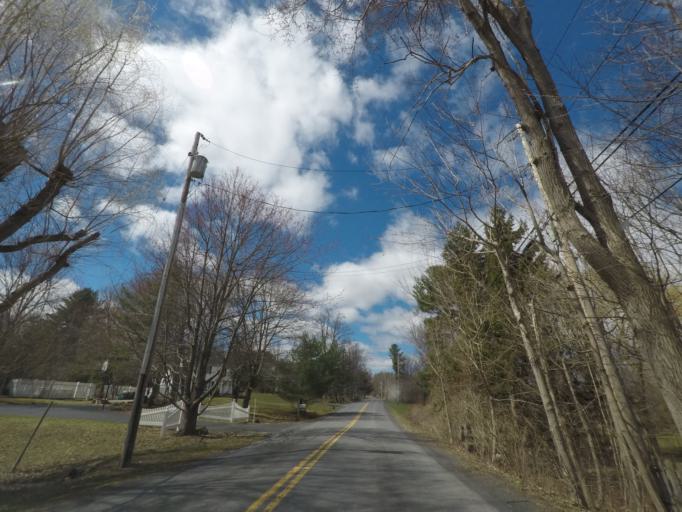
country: US
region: New York
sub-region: Albany County
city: Voorheesville
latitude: 42.6290
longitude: -73.9225
